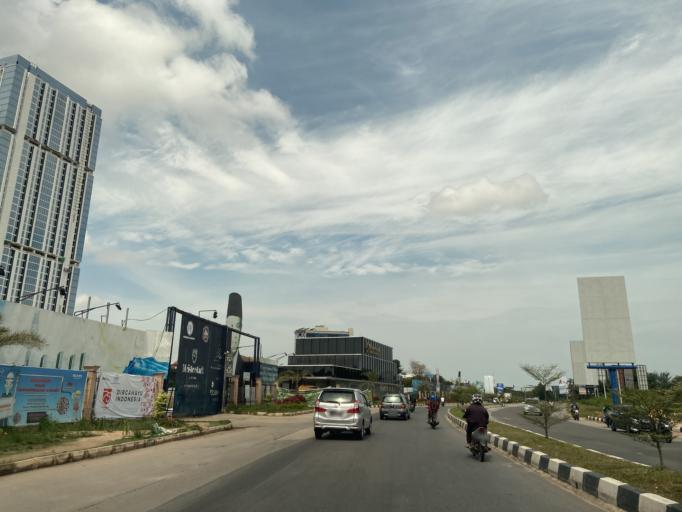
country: SG
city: Singapore
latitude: 1.1192
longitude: 104.0438
